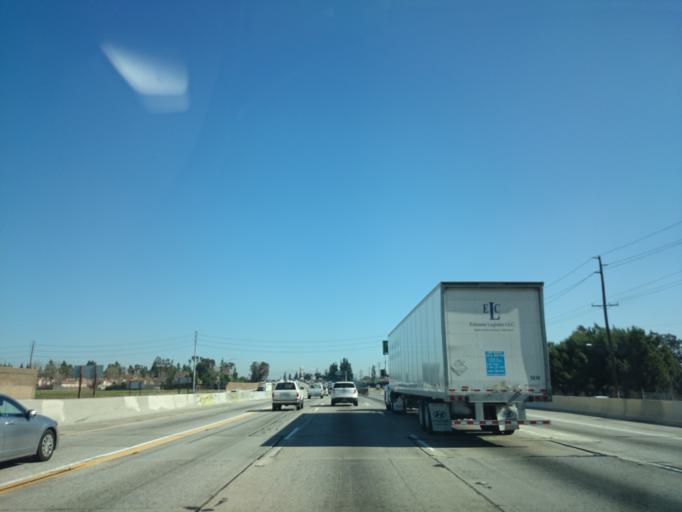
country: US
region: California
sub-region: San Bernardino County
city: Montclair
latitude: 34.0817
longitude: -117.7049
